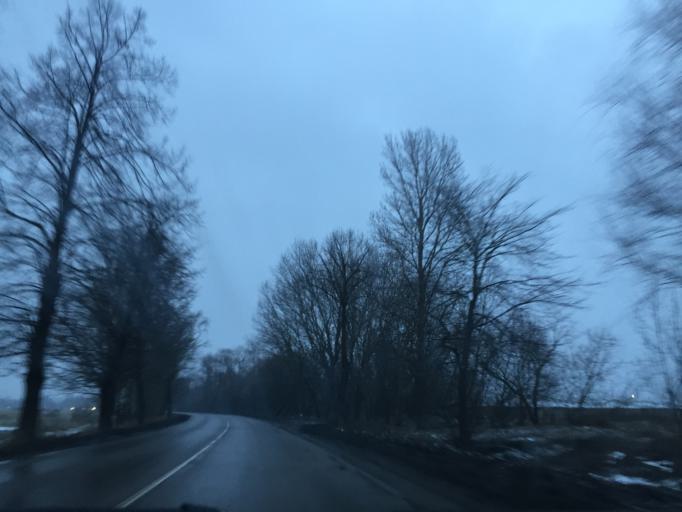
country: LV
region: Riga
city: Riga
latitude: 56.9805
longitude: 24.0830
